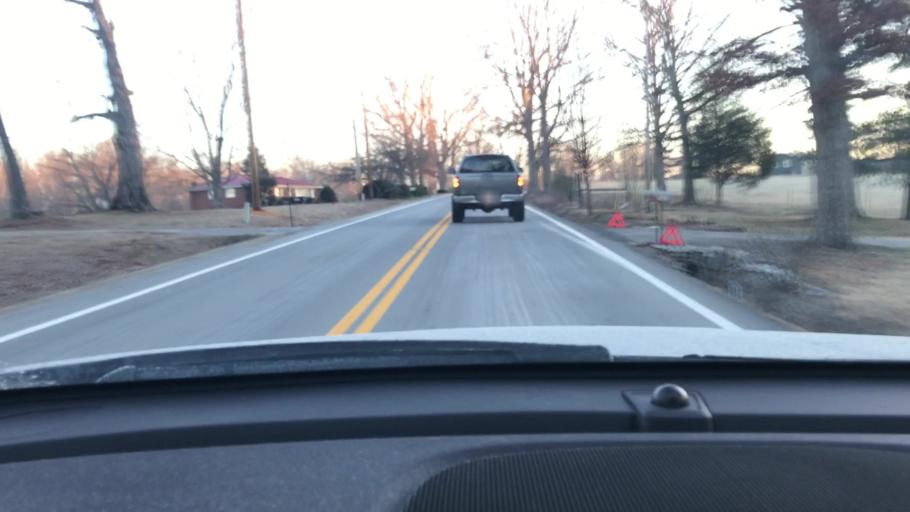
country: US
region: Tennessee
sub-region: Dickson County
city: Charlotte
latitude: 36.2240
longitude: -87.2589
